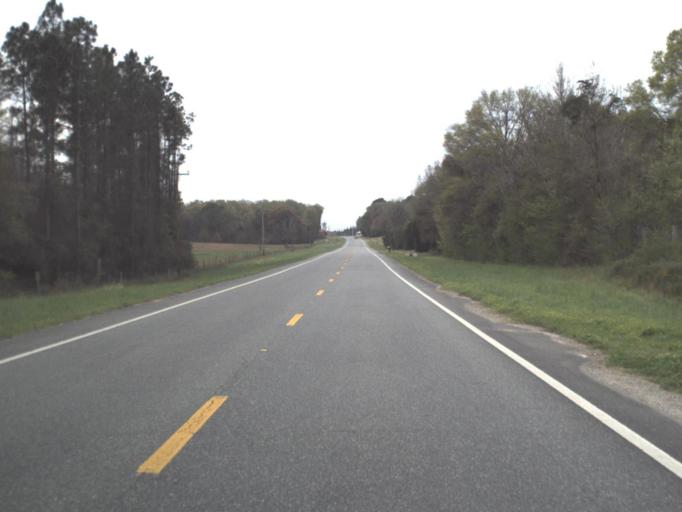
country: US
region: Florida
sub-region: Calhoun County
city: Blountstown
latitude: 30.5432
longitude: -85.1898
